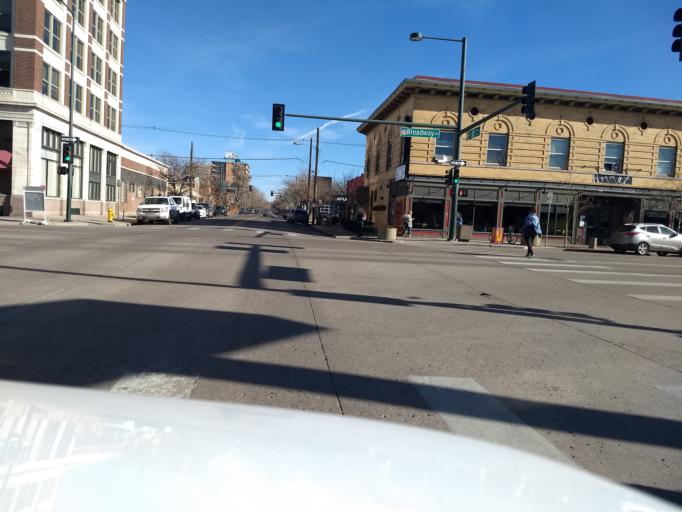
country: US
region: Colorado
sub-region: Denver County
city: Denver
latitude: 39.7184
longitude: -104.9877
